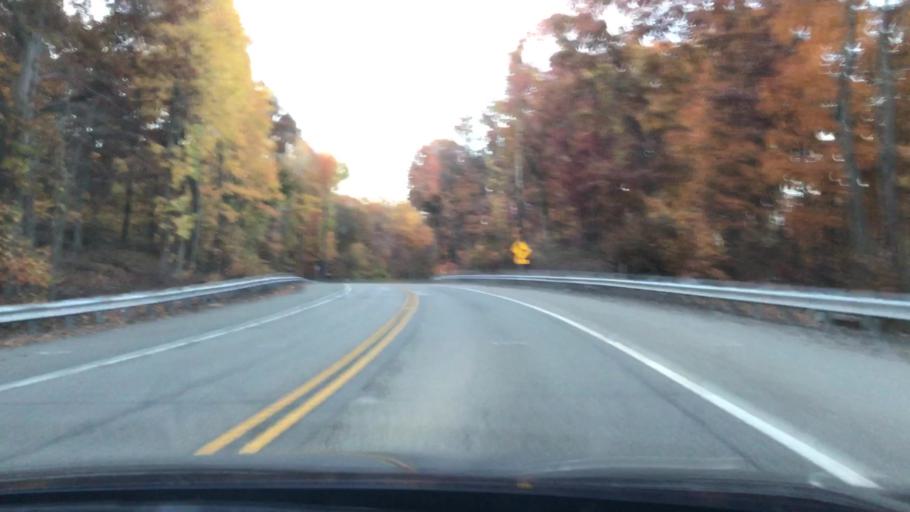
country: US
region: New Jersey
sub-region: Bergen County
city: Tenafly
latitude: 40.9128
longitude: -73.9353
